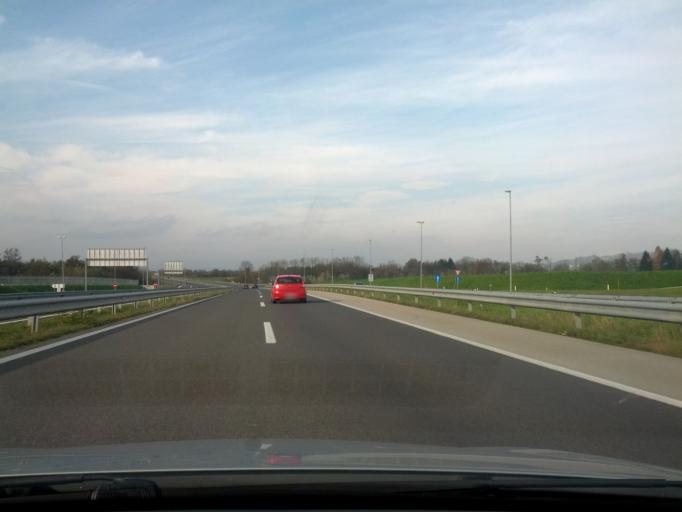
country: HR
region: Zagrebacka
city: Bregana
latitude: 45.8566
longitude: 15.6843
